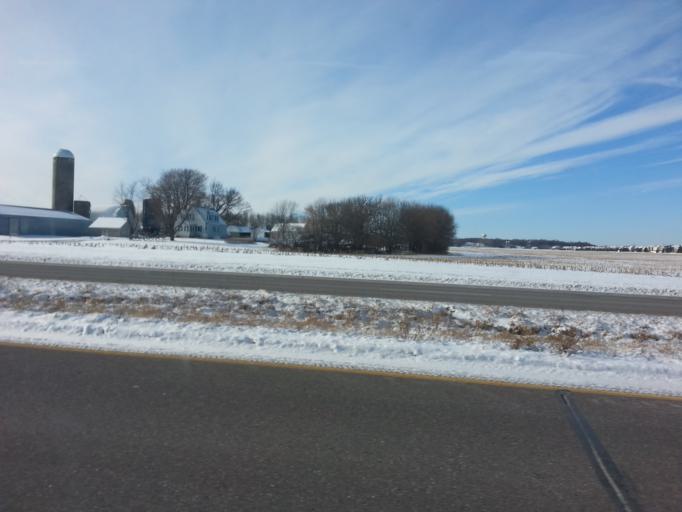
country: US
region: Minnesota
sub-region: Scott County
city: Prior Lake
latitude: 44.7589
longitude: -93.4695
